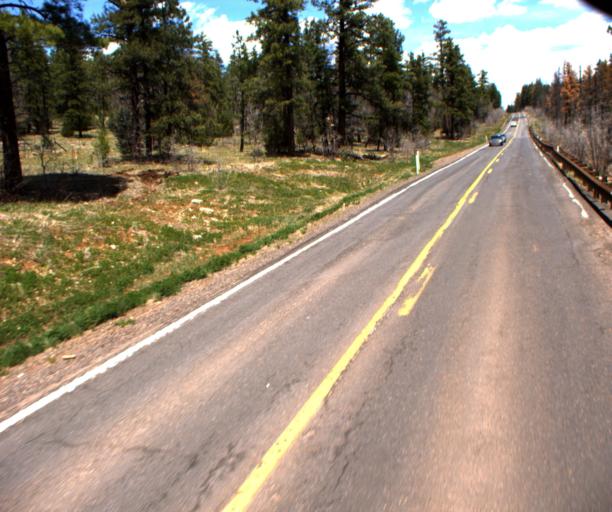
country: US
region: Arizona
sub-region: Coconino County
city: Kachina Village
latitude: 35.0535
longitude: -111.7327
